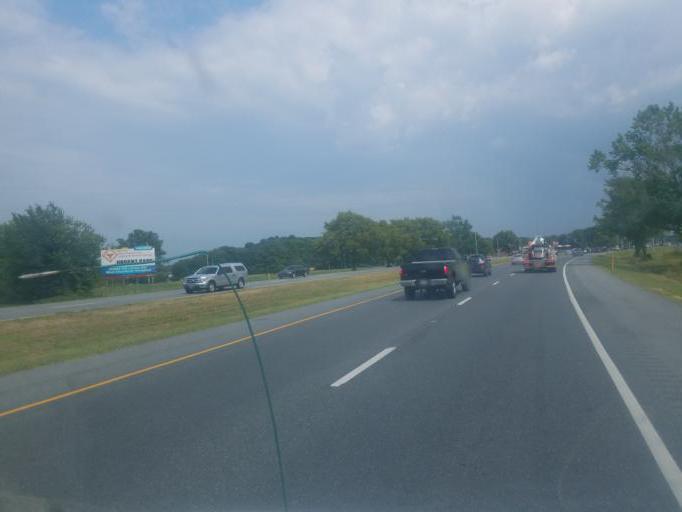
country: US
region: Maryland
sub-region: Worcester County
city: Ocean Pines
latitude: 38.3472
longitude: -75.1708
